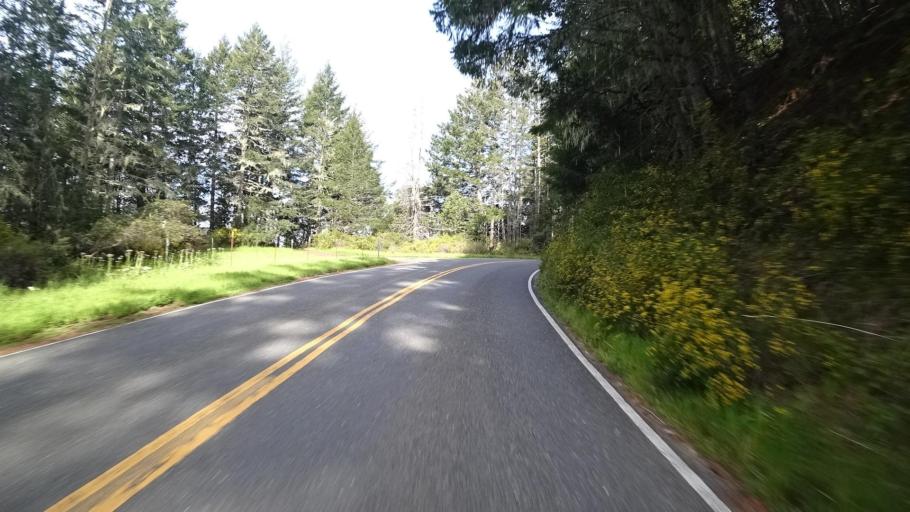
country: US
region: California
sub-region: Humboldt County
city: Blue Lake
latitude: 40.7427
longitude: -123.9615
